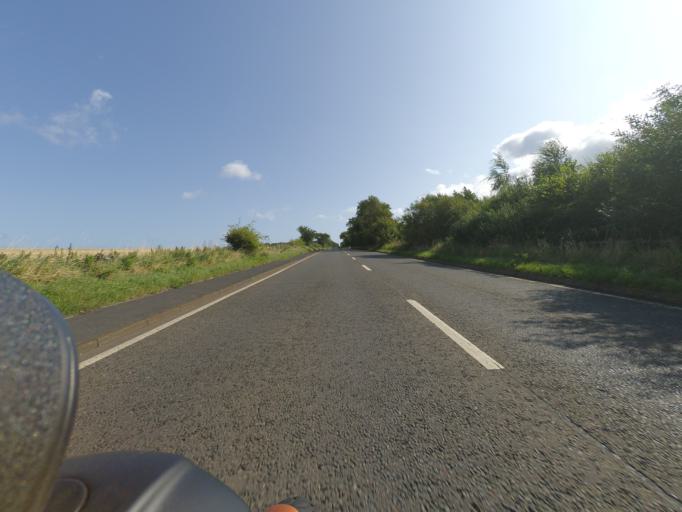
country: GB
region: Scotland
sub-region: East Lothian
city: East Linton
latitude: 55.9767
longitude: -2.6992
